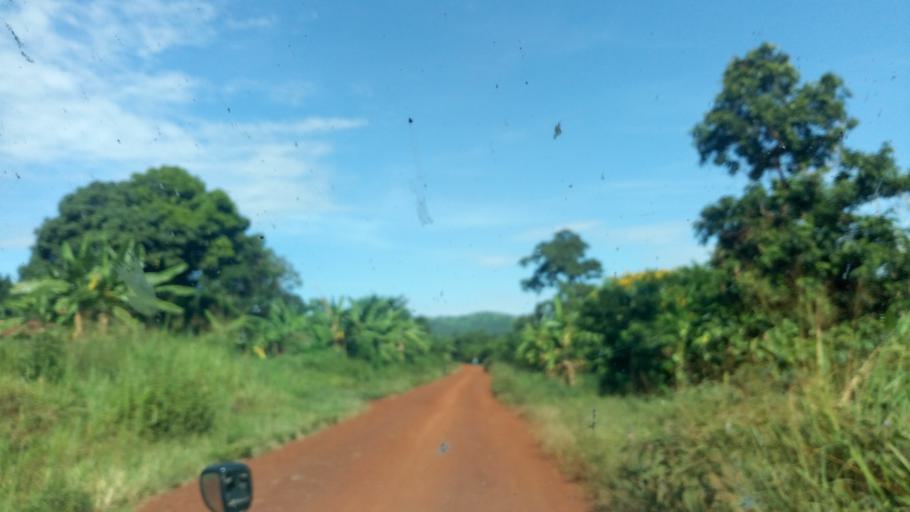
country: UG
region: Western Region
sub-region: Masindi District
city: Masindi
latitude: 1.6417
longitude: 31.7601
